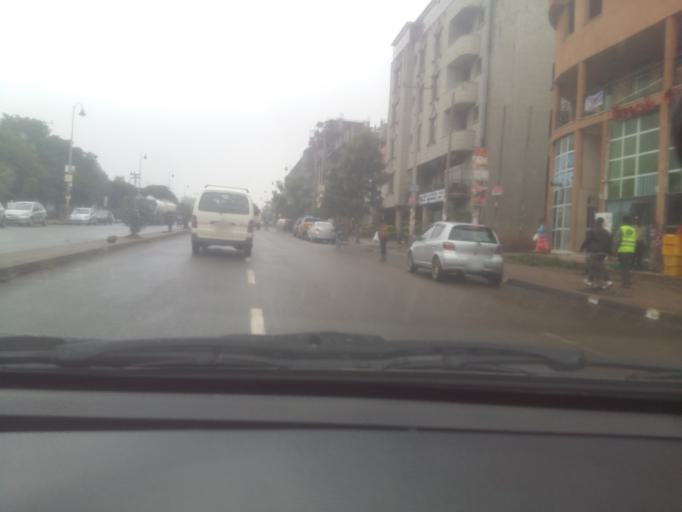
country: ET
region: Adis Abeba
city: Addis Ababa
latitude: 8.9526
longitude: 38.7160
